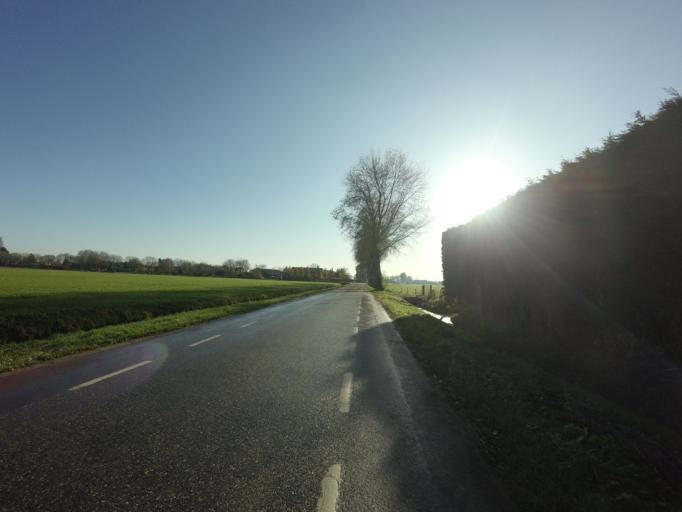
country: NL
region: Gelderland
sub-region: Gemeente Zaltbommel
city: Zaltbommel
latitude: 51.7895
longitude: 5.2723
